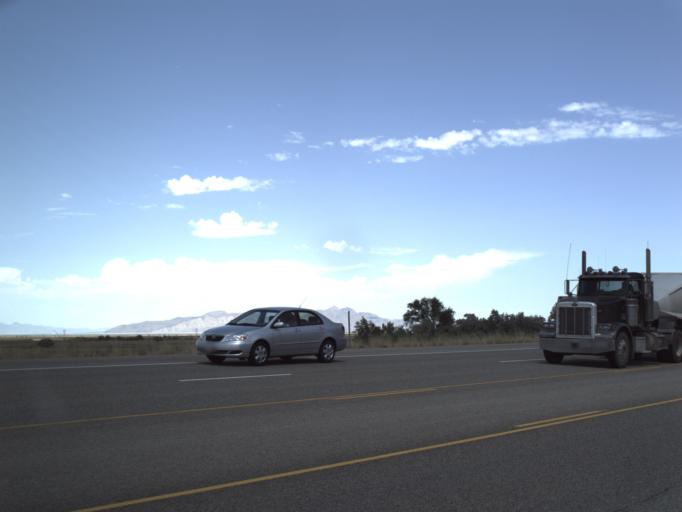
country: US
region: Utah
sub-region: Tooele County
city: Stansbury park
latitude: 40.6549
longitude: -112.2893
